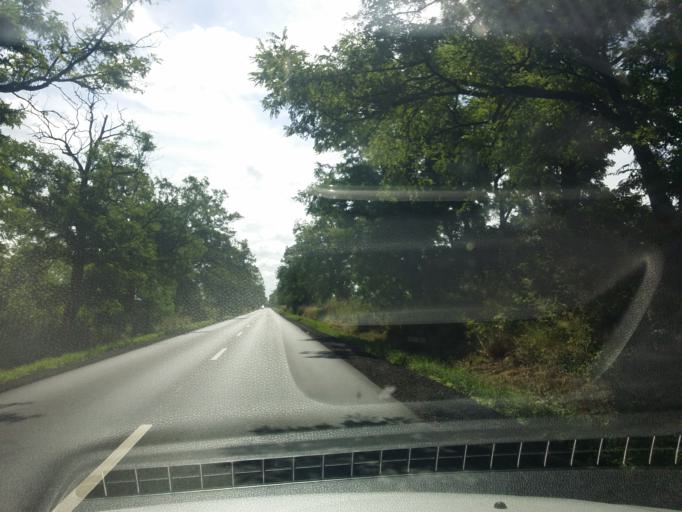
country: HU
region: Heves
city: Heves
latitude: 47.6238
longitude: 20.2507
